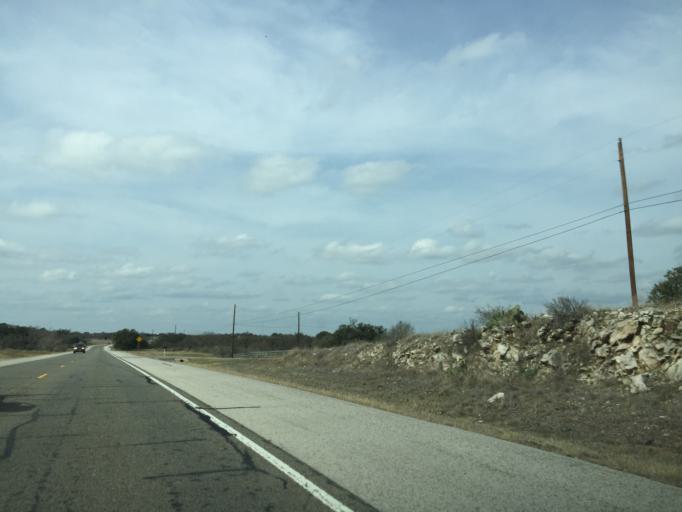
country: US
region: Texas
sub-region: Llano County
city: Horseshoe Bay
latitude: 30.5157
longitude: -98.3993
